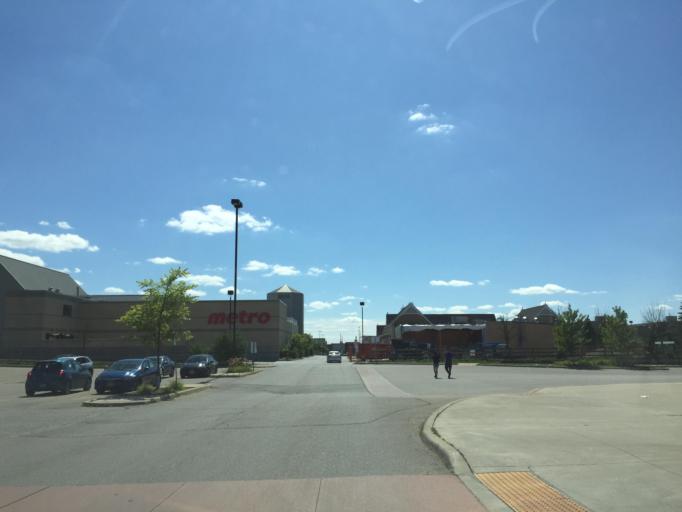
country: CA
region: Ontario
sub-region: Wellington County
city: Guelph
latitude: 43.5226
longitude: -80.2330
